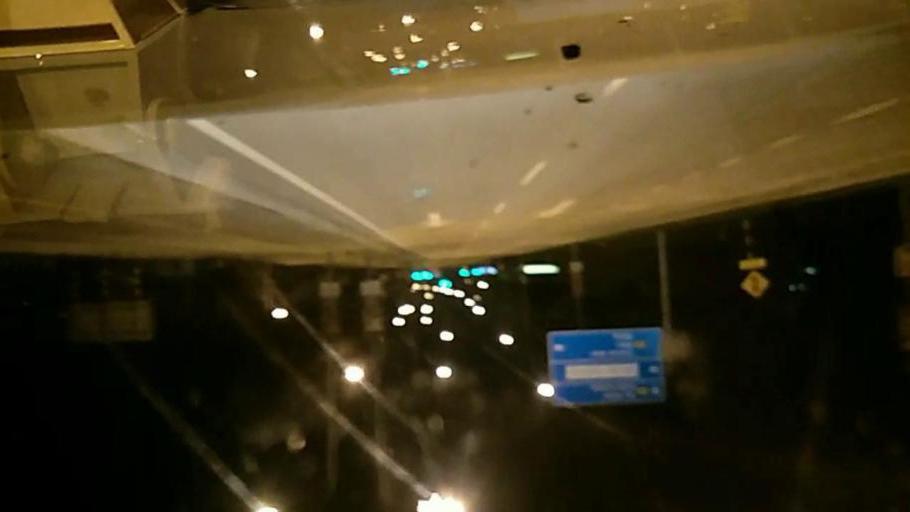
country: MY
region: Selangor
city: Ladang Seri Kundang
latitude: 3.2492
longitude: 101.4713
